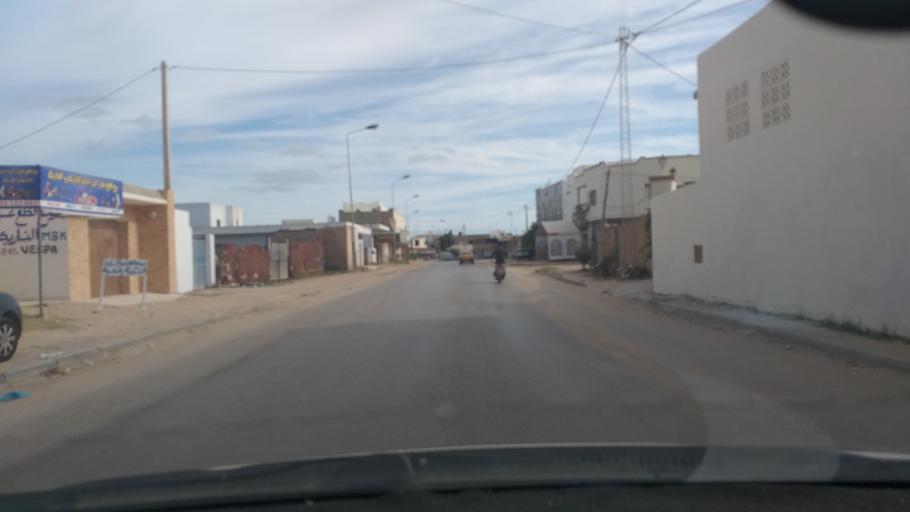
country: TN
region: Safaqis
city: Al Qarmadah
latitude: 34.7945
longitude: 10.8021
